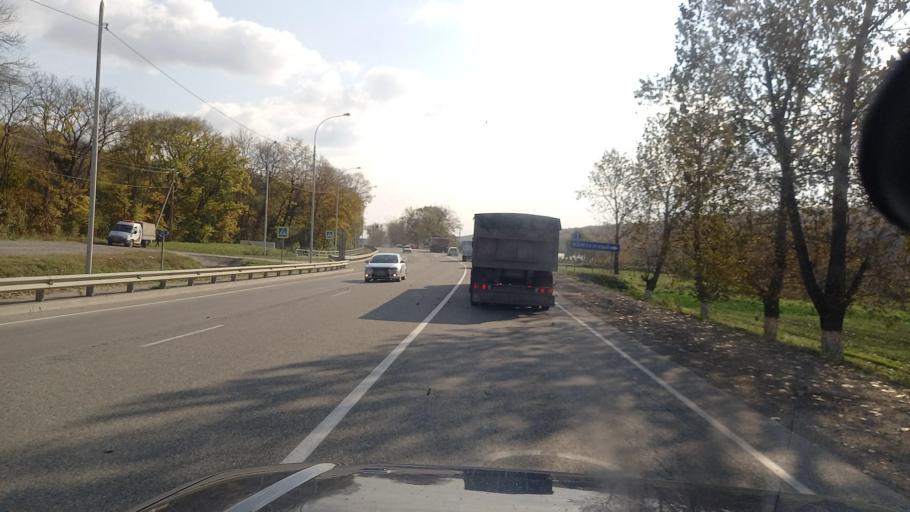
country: RU
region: Krasnodarskiy
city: Gayduk
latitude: 44.8751
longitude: 37.7878
